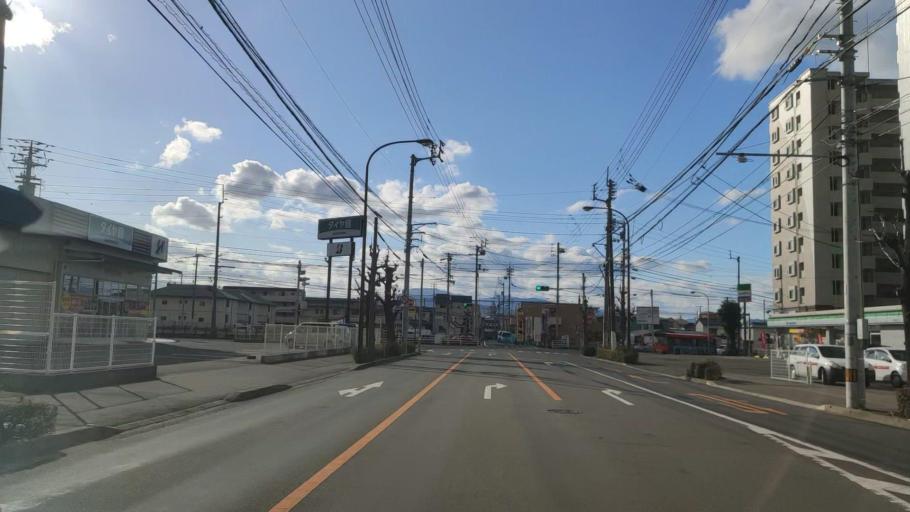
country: JP
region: Ehime
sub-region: Shikoku-chuo Shi
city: Matsuyama
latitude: 33.8309
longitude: 132.7525
